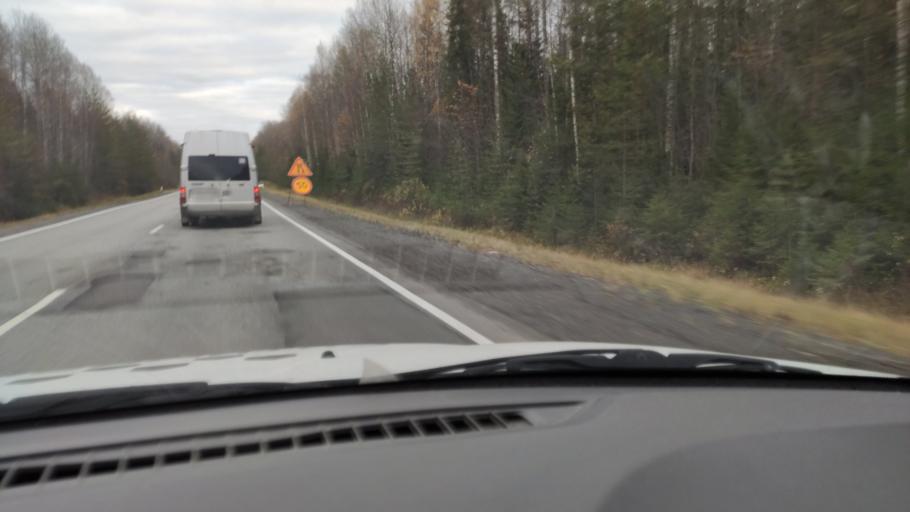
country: RU
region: Kirov
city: Chernaya Kholunitsa
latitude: 58.8588
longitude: 51.6449
